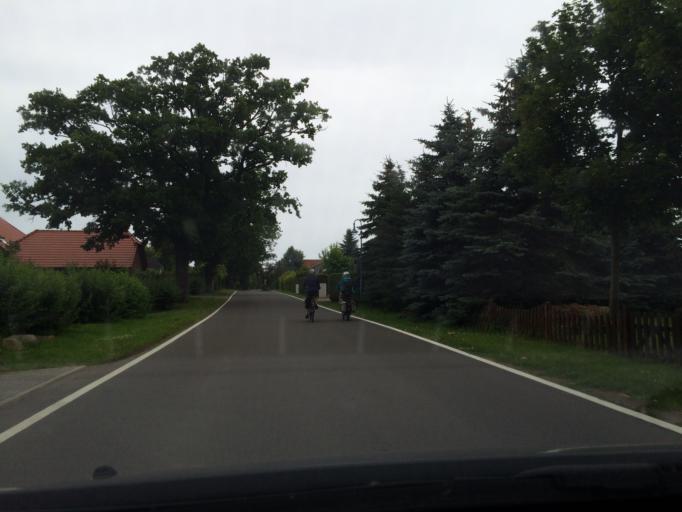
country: DE
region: Mecklenburg-Vorpommern
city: Prohn
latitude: 54.4138
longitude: 13.0149
